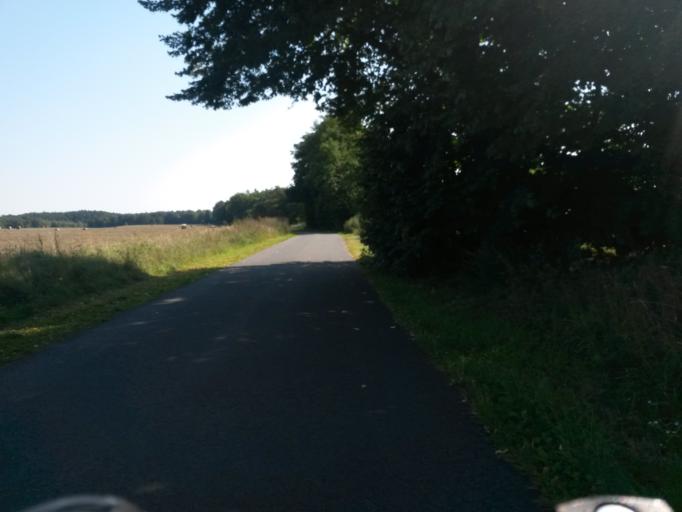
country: DE
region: Brandenburg
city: Templin
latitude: 53.0449
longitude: 13.4967
